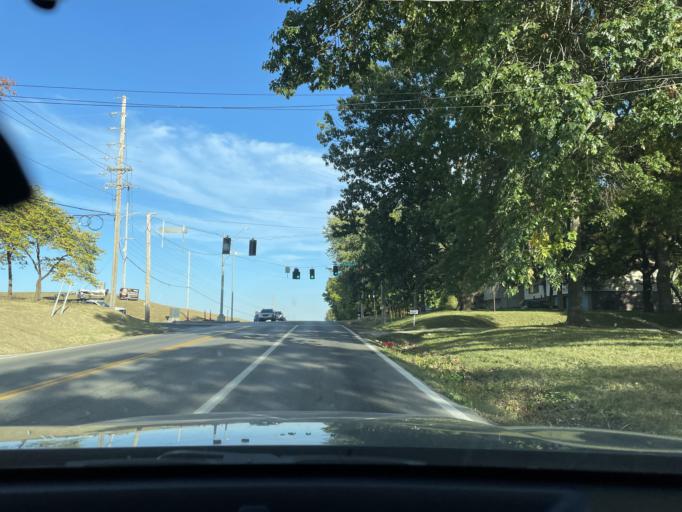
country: US
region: Missouri
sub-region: Buchanan County
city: Saint Joseph
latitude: 39.7552
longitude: -94.7972
